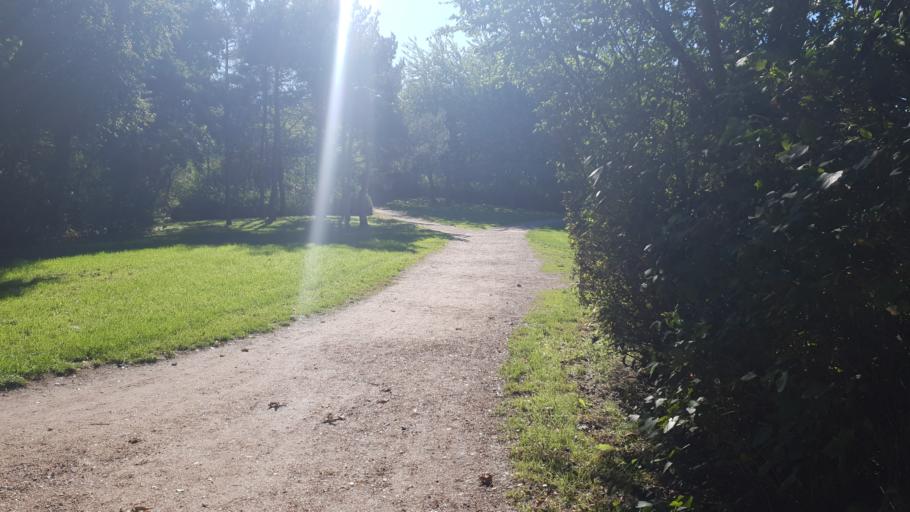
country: DK
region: Zealand
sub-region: Roskilde Kommune
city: Roskilde
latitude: 55.6321
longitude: 12.0834
